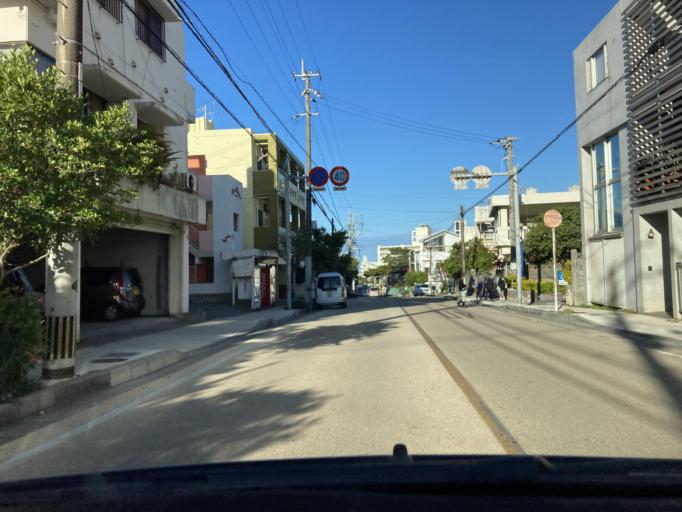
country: JP
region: Okinawa
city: Naha-shi
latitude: 26.2096
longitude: 127.7139
